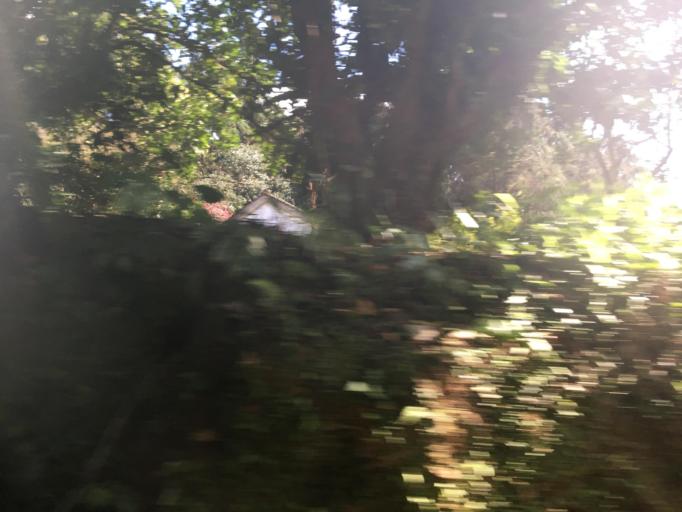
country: TW
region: Taiwan
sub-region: Yilan
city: Yilan
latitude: 24.7550
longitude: 121.6233
